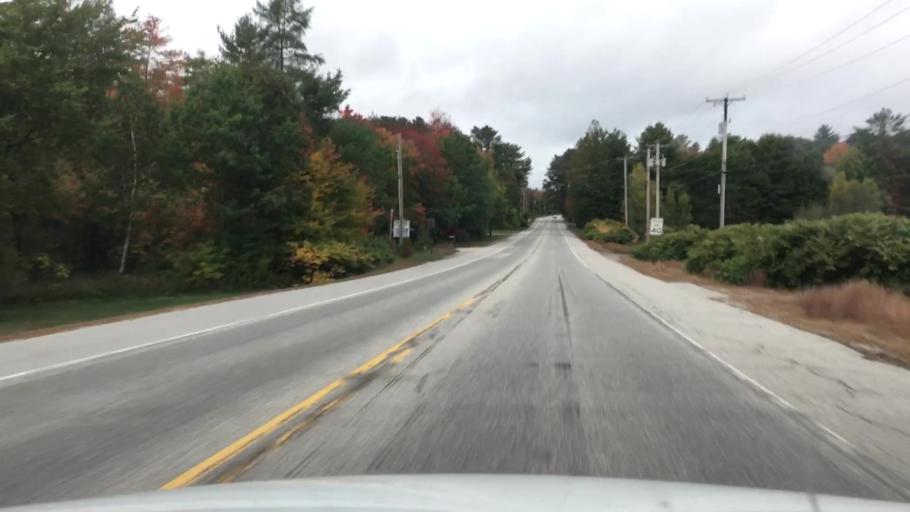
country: US
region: Maine
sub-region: Oxford County
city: Oxford
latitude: 44.1267
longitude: -70.4538
